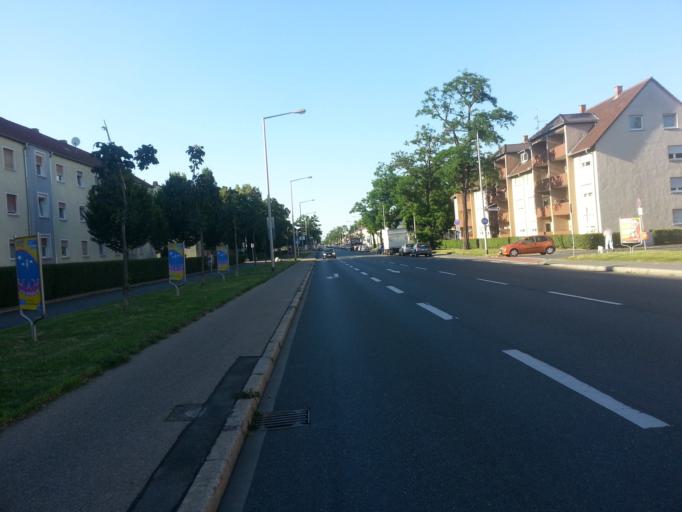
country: DE
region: Baden-Wuerttemberg
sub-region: Karlsruhe Region
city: Mannheim
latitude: 49.5079
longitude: 8.5061
